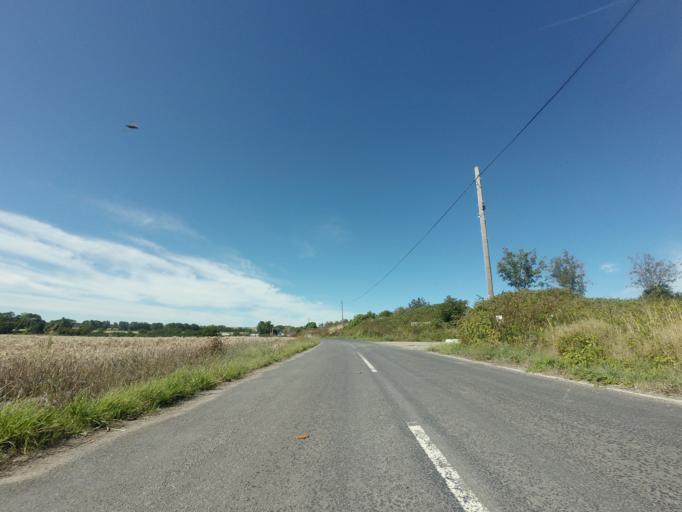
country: GB
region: England
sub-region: Kent
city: Sandwich
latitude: 51.3255
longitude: 1.3481
